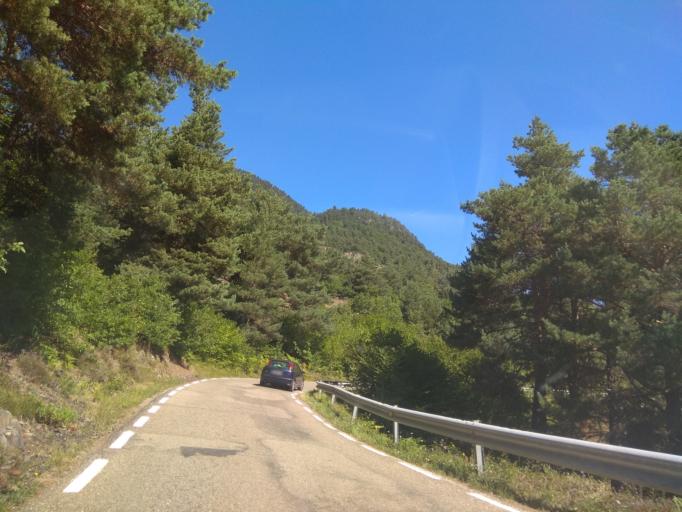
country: ES
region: Catalonia
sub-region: Provincia de Lleida
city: Vielha
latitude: 42.7404
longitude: 0.7468
